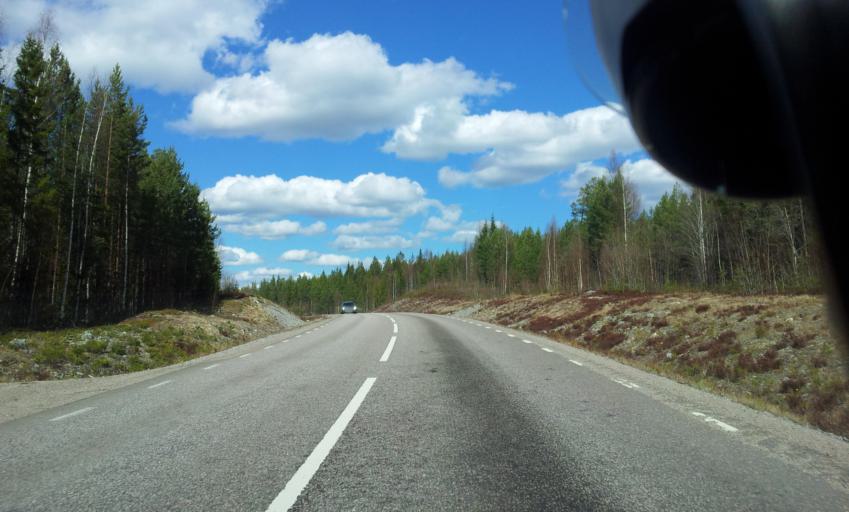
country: SE
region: Gaevleborg
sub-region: Ovanakers Kommun
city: Edsbyn
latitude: 61.2157
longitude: 15.8764
